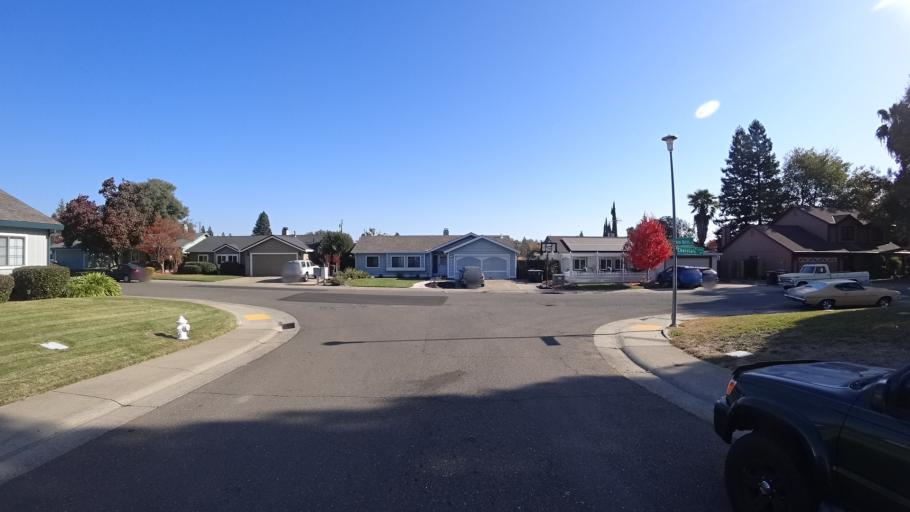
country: US
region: California
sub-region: Sacramento County
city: Citrus Heights
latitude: 38.6951
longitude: -121.2855
